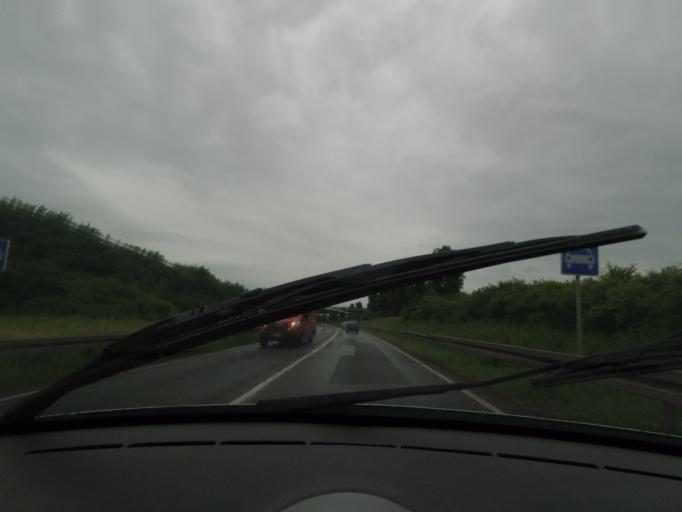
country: DE
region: Thuringia
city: Saalfeld
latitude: 50.6637
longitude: 11.3491
